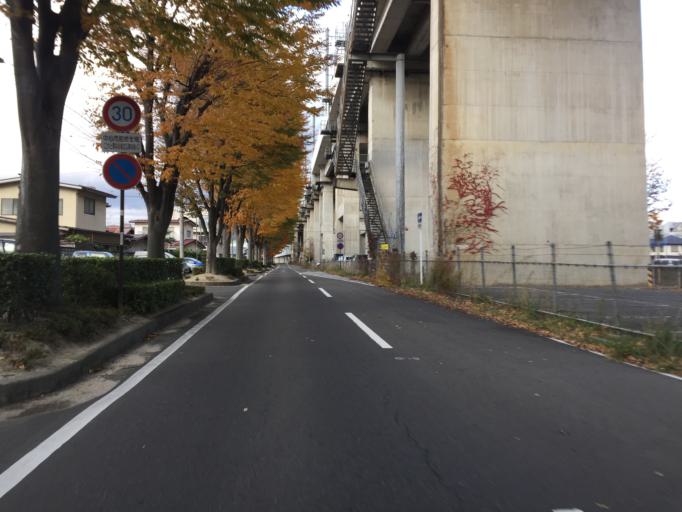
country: JP
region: Fukushima
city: Fukushima-shi
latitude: 37.7490
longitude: 140.4586
